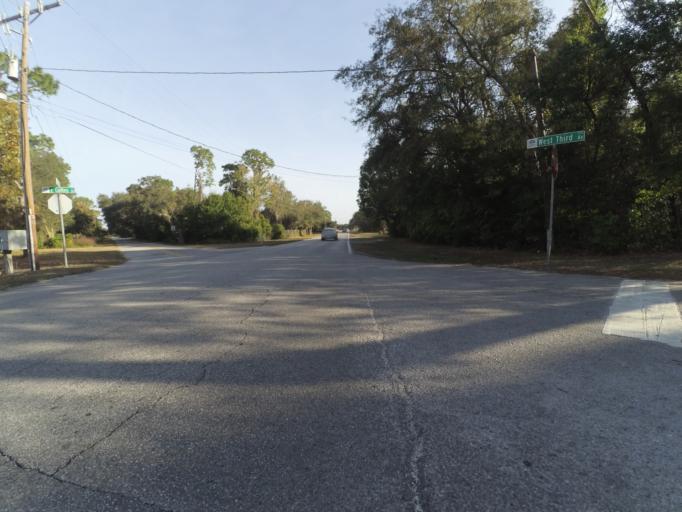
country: US
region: Florida
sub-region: Lake County
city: Umatilla
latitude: 28.9404
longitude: -81.6372
